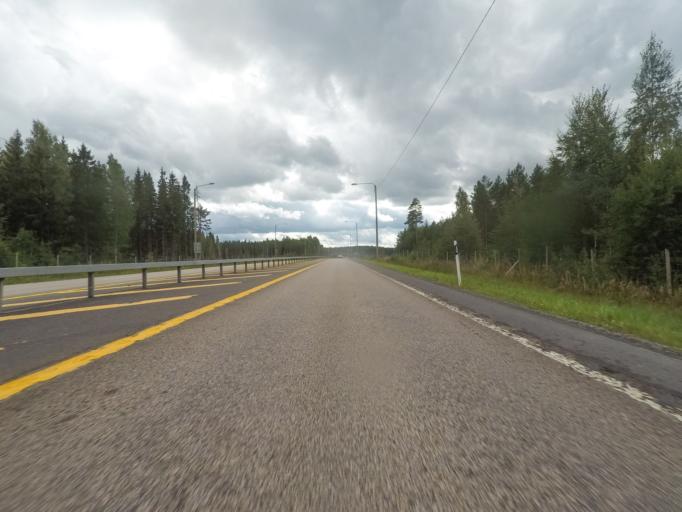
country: FI
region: Paijanne Tavastia
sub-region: Lahti
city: Hartola
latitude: 61.5293
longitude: 26.0062
